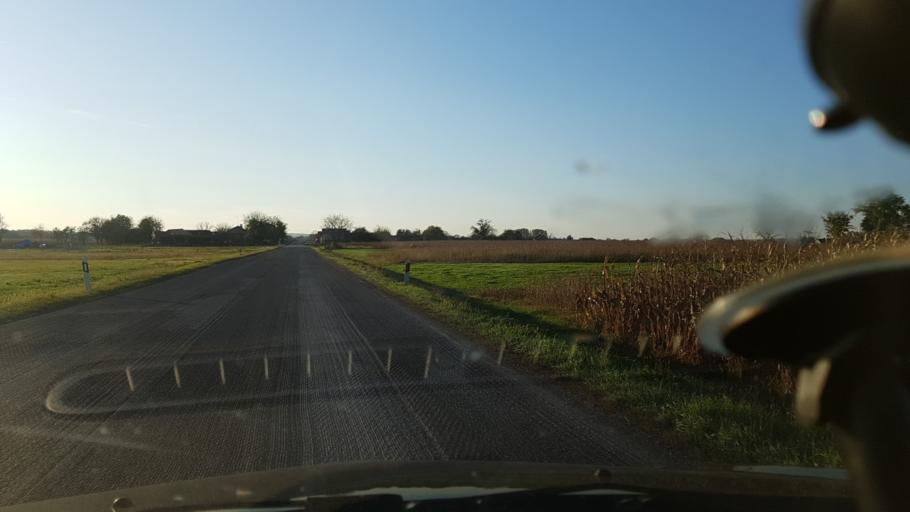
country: HR
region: Koprivnicko-Krizevacka
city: Virje
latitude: 46.0587
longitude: 17.0151
